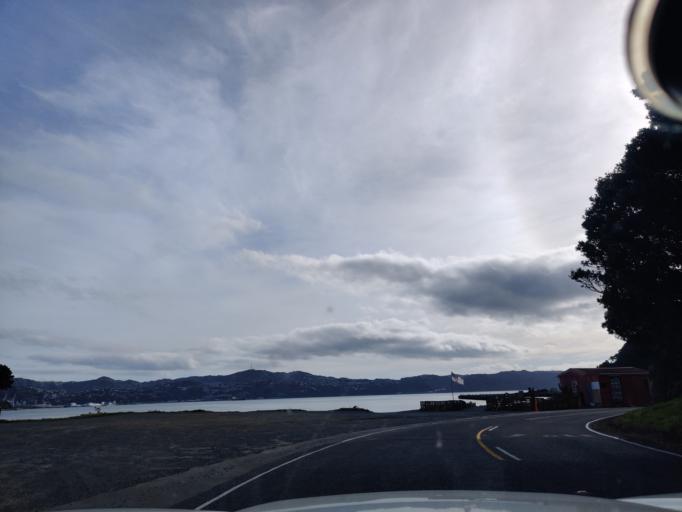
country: NZ
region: Wellington
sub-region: Wellington City
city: Wellington
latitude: -41.2979
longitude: 174.8207
